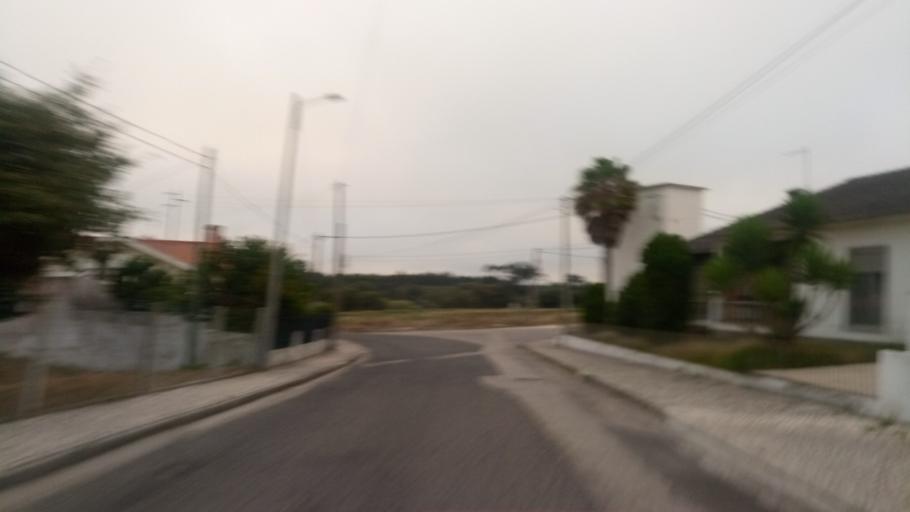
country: PT
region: Leiria
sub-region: Caldas da Rainha
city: Caldas da Rainha
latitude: 39.4285
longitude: -9.1543
